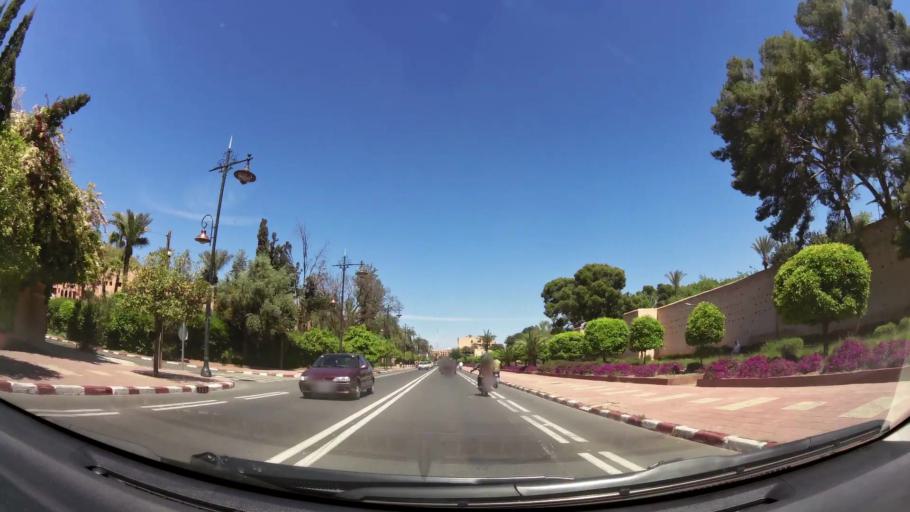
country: MA
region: Marrakech-Tensift-Al Haouz
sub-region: Marrakech
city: Marrakesh
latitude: 31.6252
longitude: -8.0009
